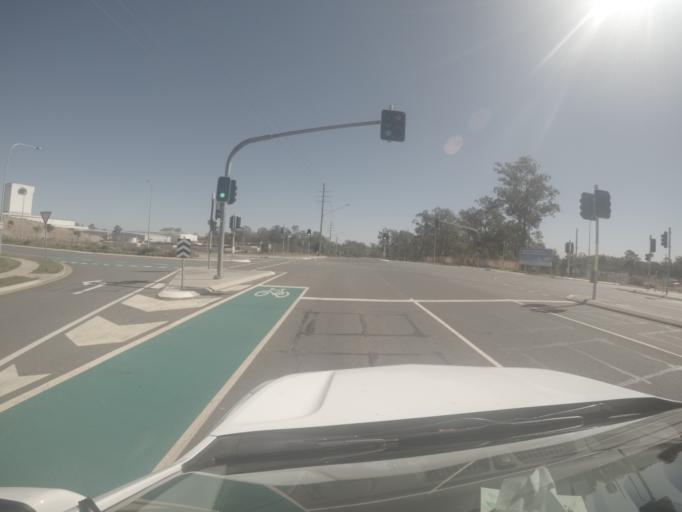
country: AU
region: Queensland
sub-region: Brisbane
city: Wacol
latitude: -27.5846
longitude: 152.9418
